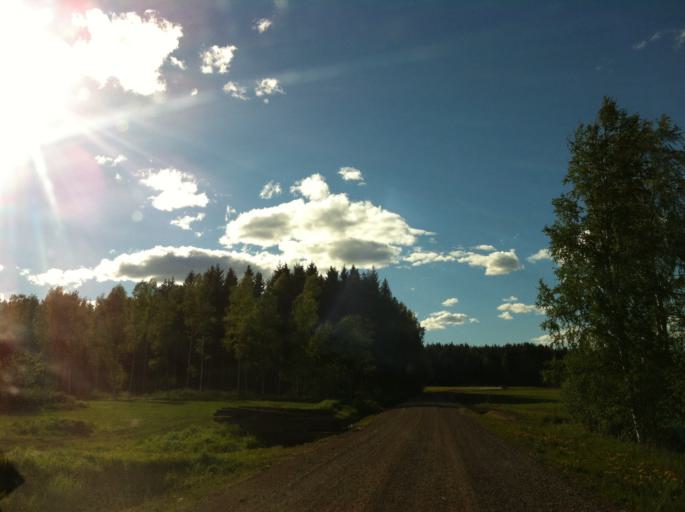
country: SE
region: Dalarna
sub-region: Leksand Municipality
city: Siljansnas
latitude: 60.7731
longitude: 14.8406
